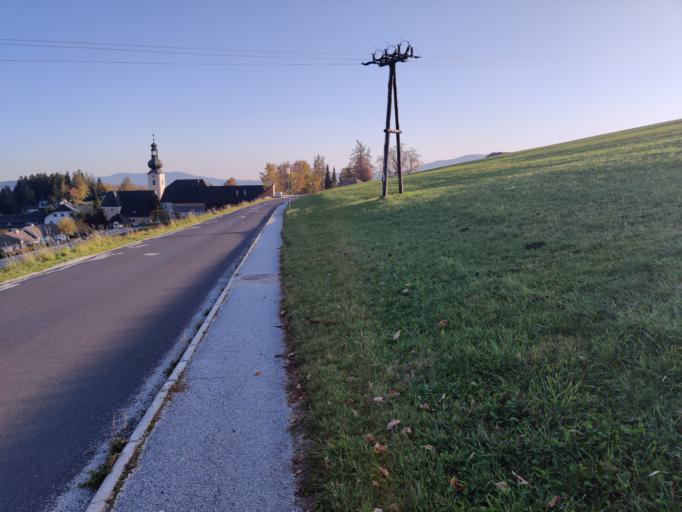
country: AT
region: Styria
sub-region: Politischer Bezirk Hartberg-Fuerstenfeld
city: Sankt Jakob im Walde
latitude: 47.4686
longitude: 15.7858
